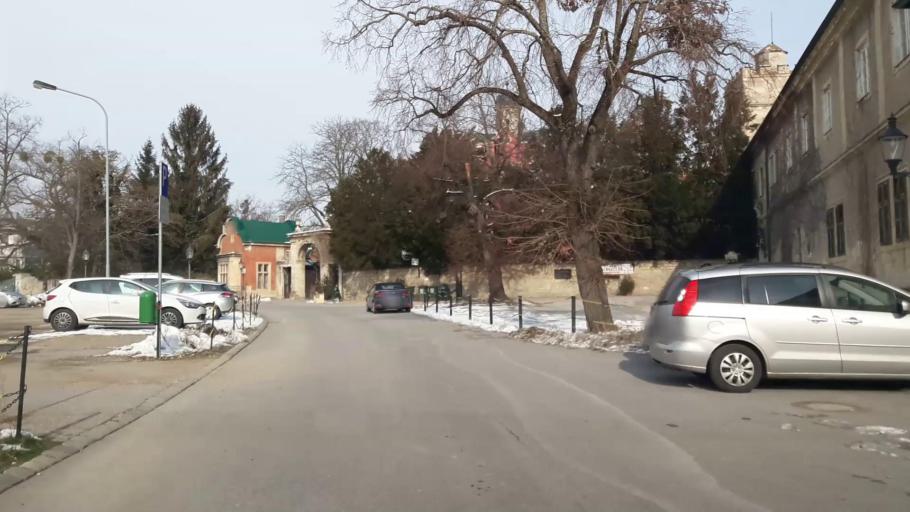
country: AT
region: Burgenland
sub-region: Politischer Bezirk Neusiedl am See
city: Bruckneudorf
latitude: 48.0249
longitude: 16.7814
